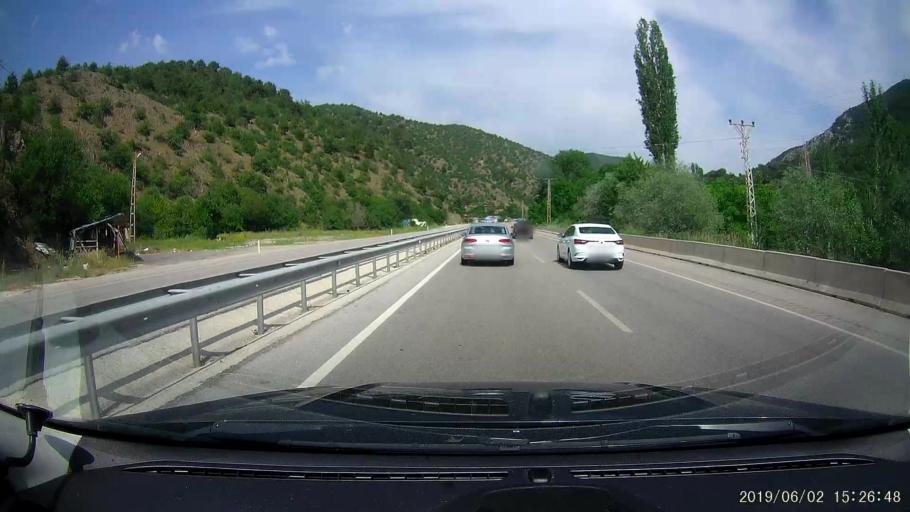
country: TR
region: Amasya
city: Saraycik
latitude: 40.9867
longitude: 35.0444
